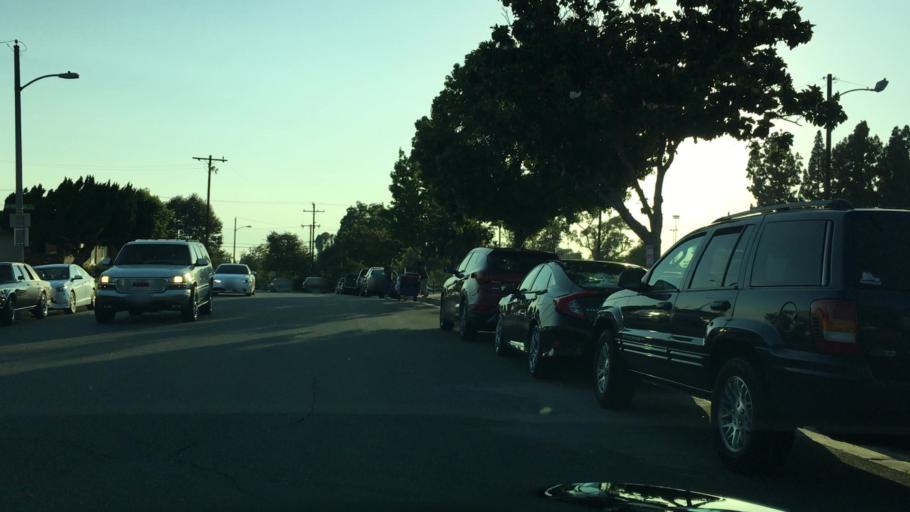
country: US
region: California
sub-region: Orange County
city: La Habra
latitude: 33.9355
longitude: -117.9579
